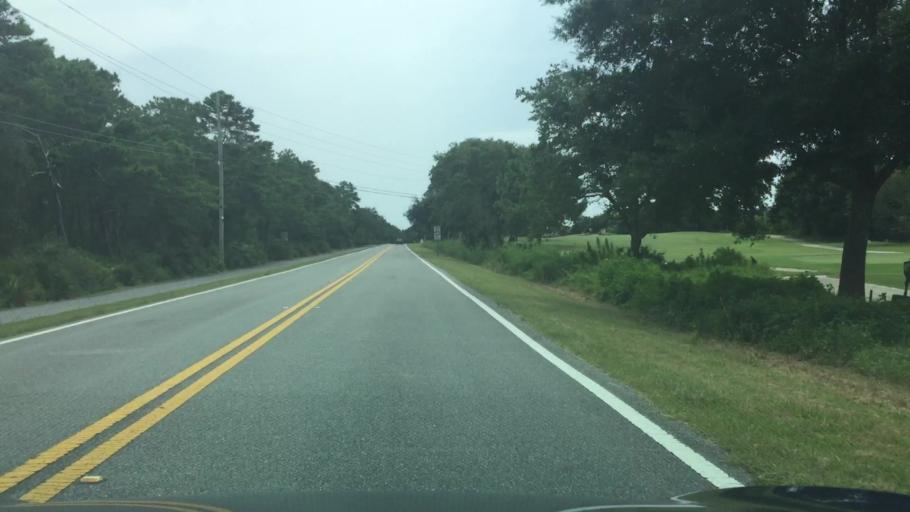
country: US
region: Florida
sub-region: Bay County
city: Upper Grand Lagoon
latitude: 30.1485
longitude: -85.7192
